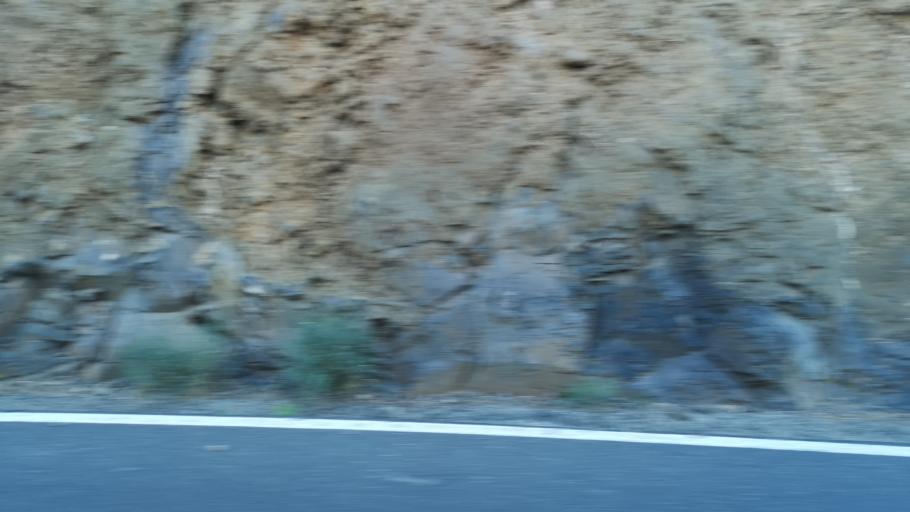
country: ES
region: Canary Islands
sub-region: Provincia de Santa Cruz de Tenerife
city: San Sebastian de la Gomera
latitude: 28.0858
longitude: -17.1212
